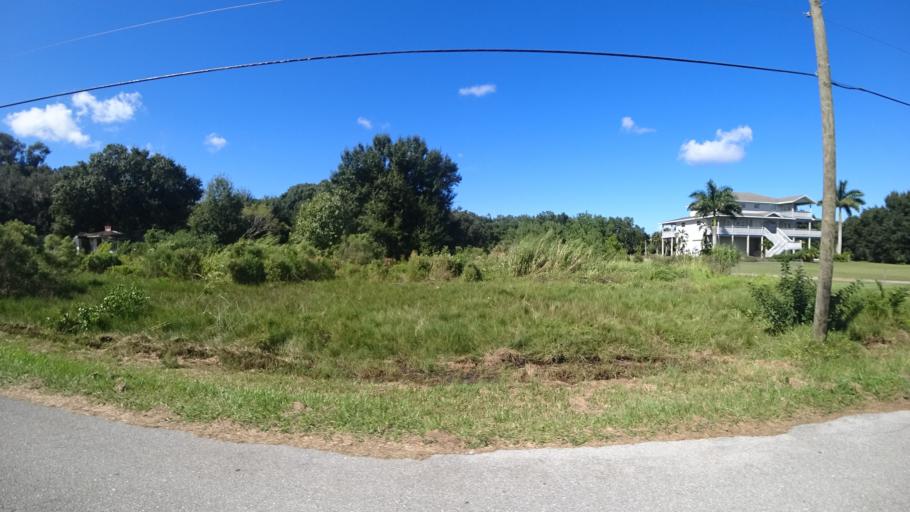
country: US
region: Florida
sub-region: Manatee County
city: Memphis
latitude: 27.5760
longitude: -82.5674
